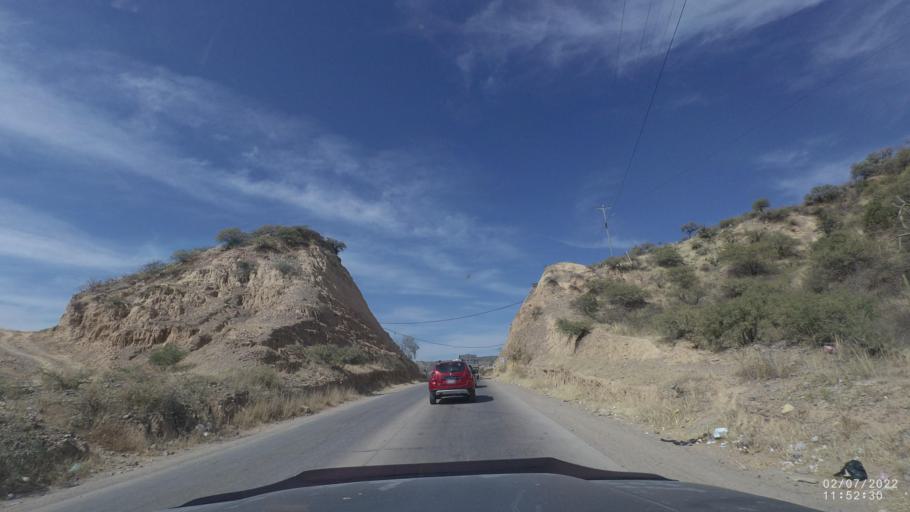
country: BO
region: Cochabamba
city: Sipe Sipe
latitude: -17.5799
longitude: -66.3341
